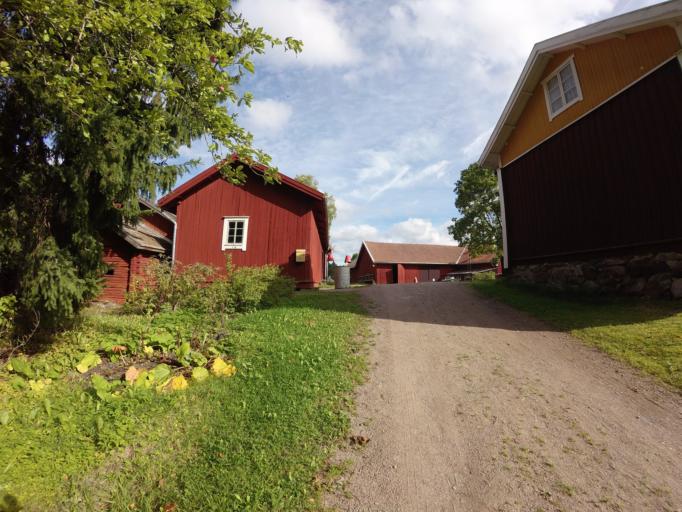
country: FI
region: Varsinais-Suomi
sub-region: Turku
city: Kaarina
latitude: 60.4624
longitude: 22.3362
